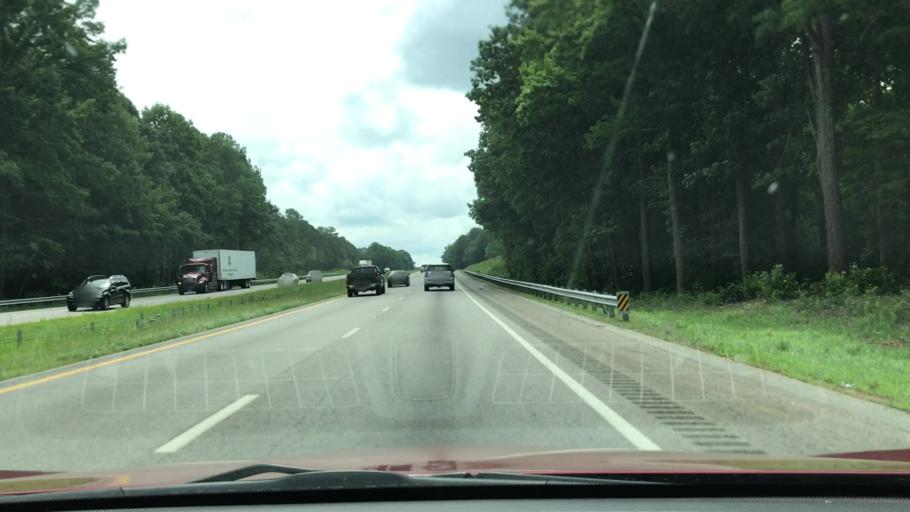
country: US
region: South Carolina
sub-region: Laurens County
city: Joanna
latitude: 34.4577
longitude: -81.7909
